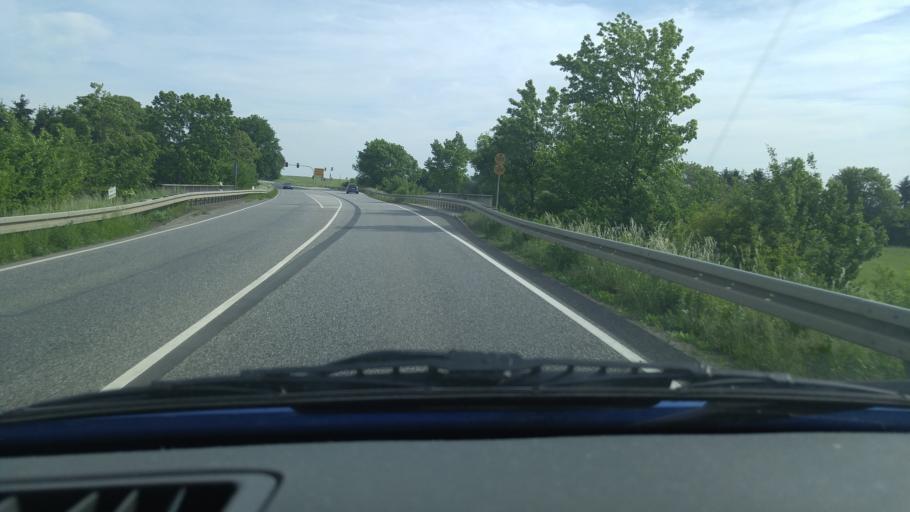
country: DE
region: Hesse
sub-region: Regierungsbezirk Darmstadt
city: Echzell
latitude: 50.4247
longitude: 8.8722
